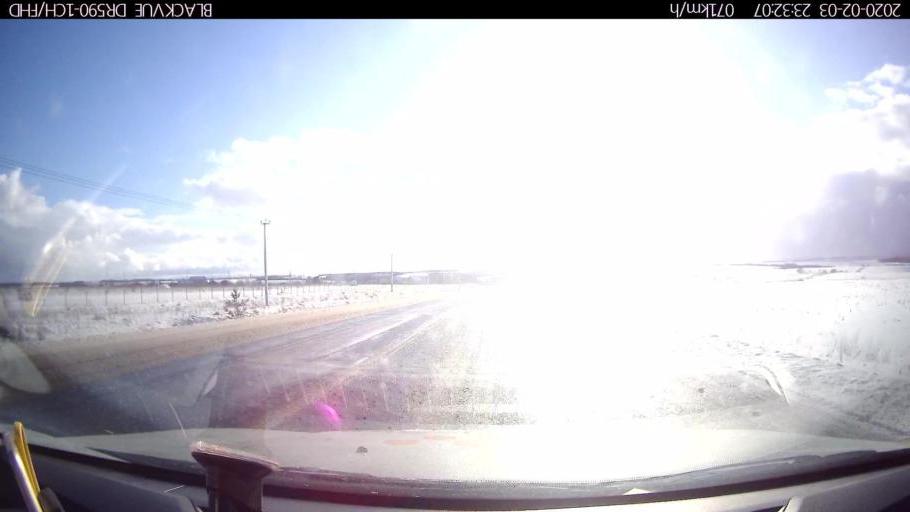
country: RU
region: Nizjnij Novgorod
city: Dal'neye Konstantinovo
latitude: 55.9351
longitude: 44.2295
